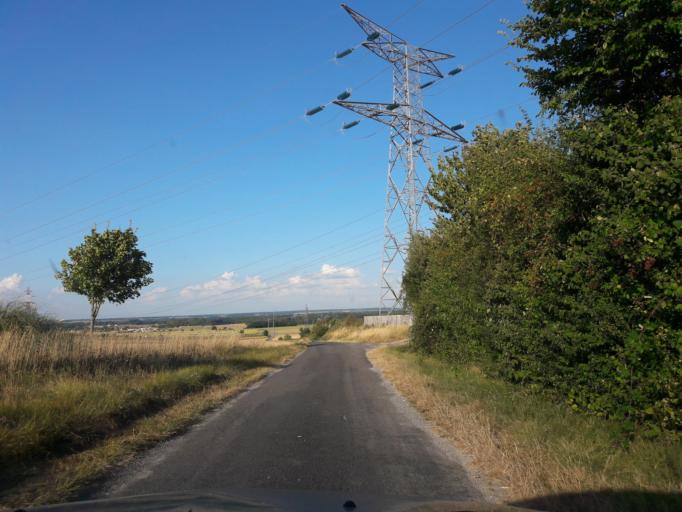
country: FR
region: Poitou-Charentes
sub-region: Departement de la Charente-Maritime
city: Thenac
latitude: 45.6637
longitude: -0.6085
